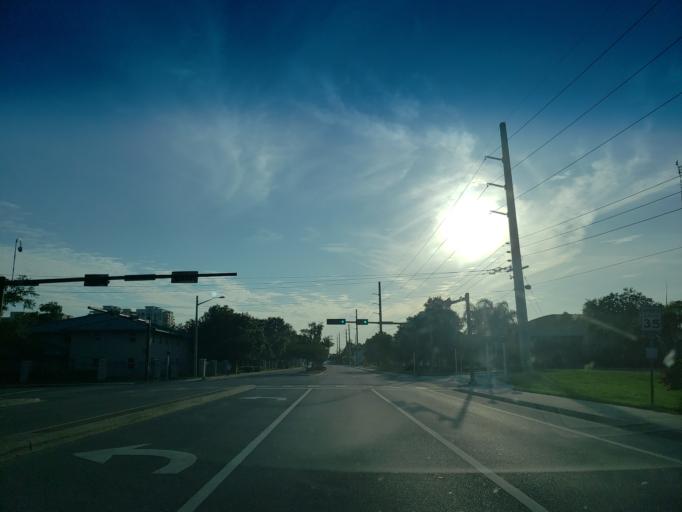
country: US
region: Florida
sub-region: Sarasota County
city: Sarasota
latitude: 27.3448
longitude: -82.5402
